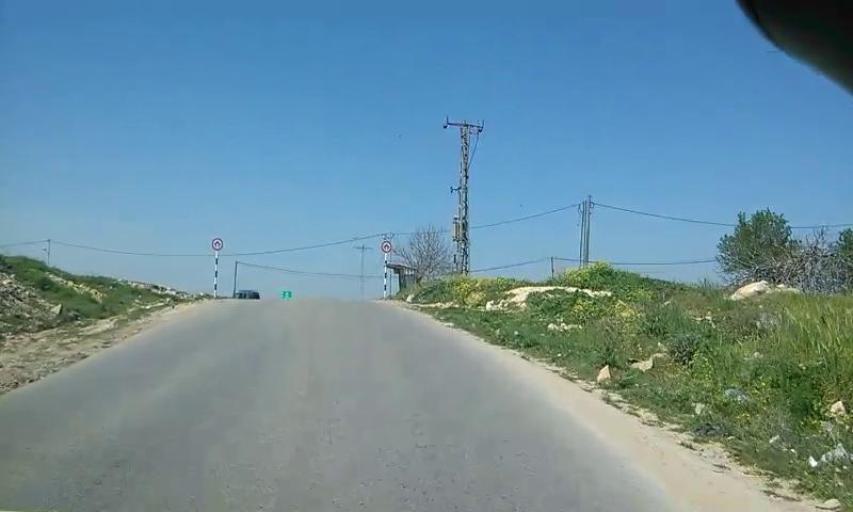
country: PS
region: West Bank
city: Battir
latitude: 31.7080
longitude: 35.1529
